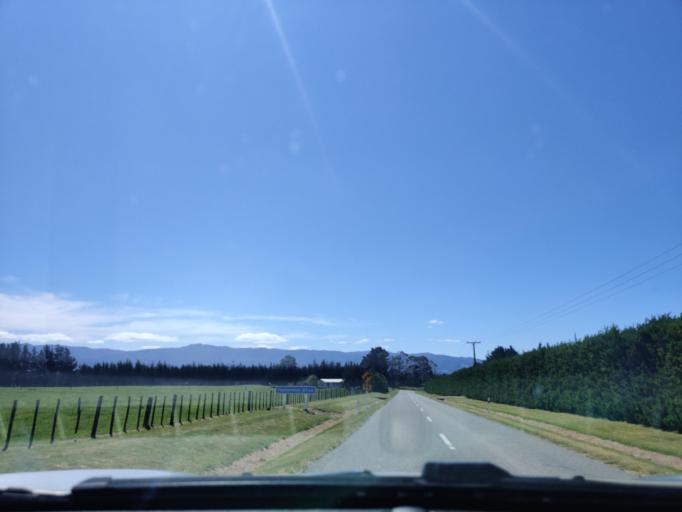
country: NZ
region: Wellington
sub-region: South Wairarapa District
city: Waipawa
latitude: -41.3040
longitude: 175.2723
